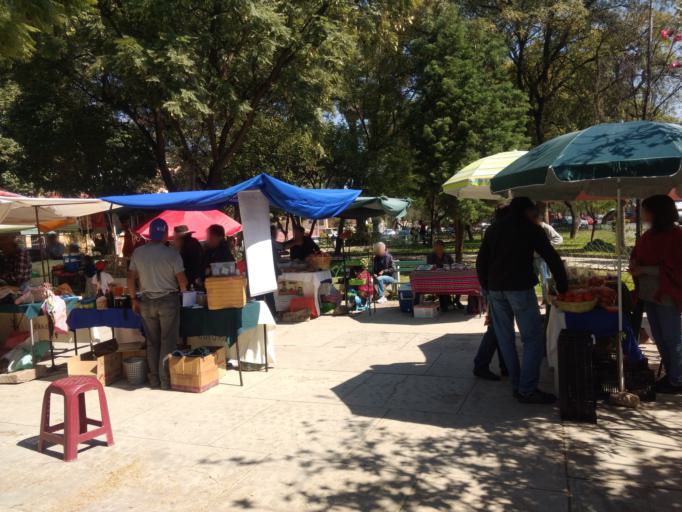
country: BO
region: Cochabamba
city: Cochabamba
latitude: -17.3879
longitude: -66.1467
